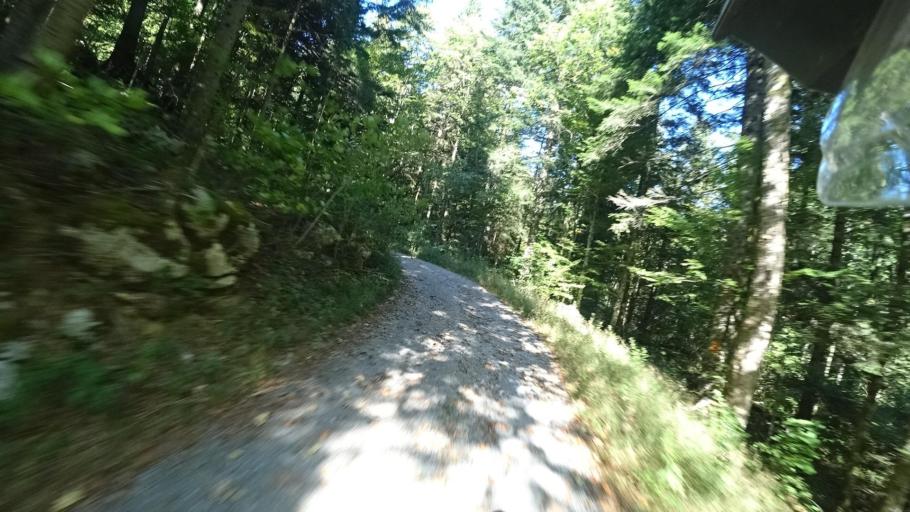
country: HR
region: Primorsko-Goranska
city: Vrbovsko
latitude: 45.2706
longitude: 15.1025
